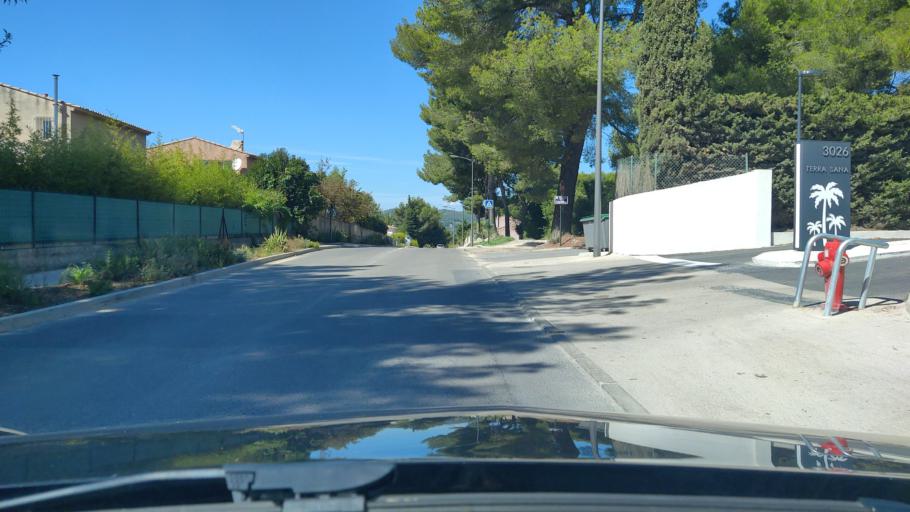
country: FR
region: Provence-Alpes-Cote d'Azur
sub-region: Departement du Var
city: Sanary-sur-Mer
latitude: 43.1338
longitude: 5.7899
